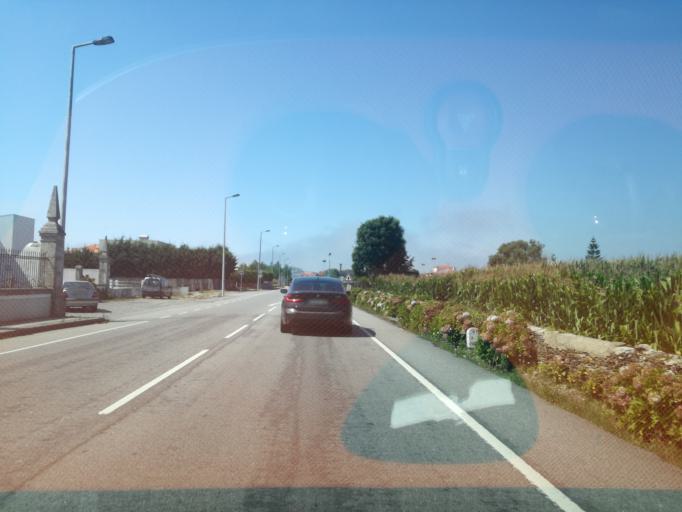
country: PT
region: Braga
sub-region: Esposende
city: Apulia
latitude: 41.5075
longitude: -8.7654
